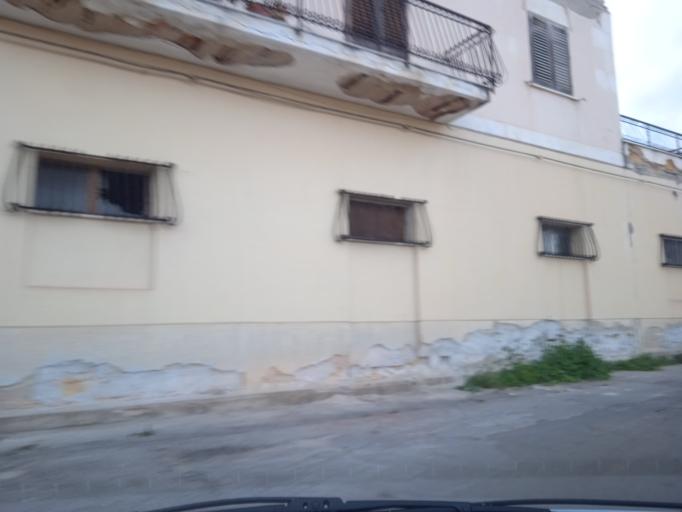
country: IT
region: Sicily
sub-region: Palermo
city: Santa Flavia
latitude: 38.0922
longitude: 13.5397
